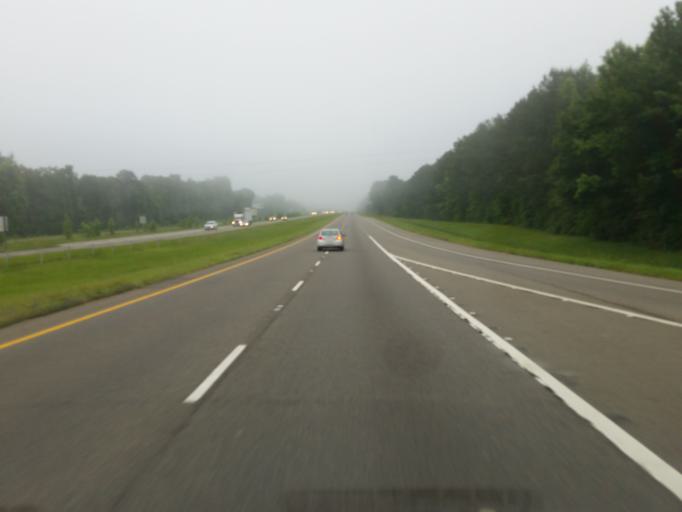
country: US
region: Louisiana
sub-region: Bossier Parish
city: Haughton
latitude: 32.5791
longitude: -93.4285
